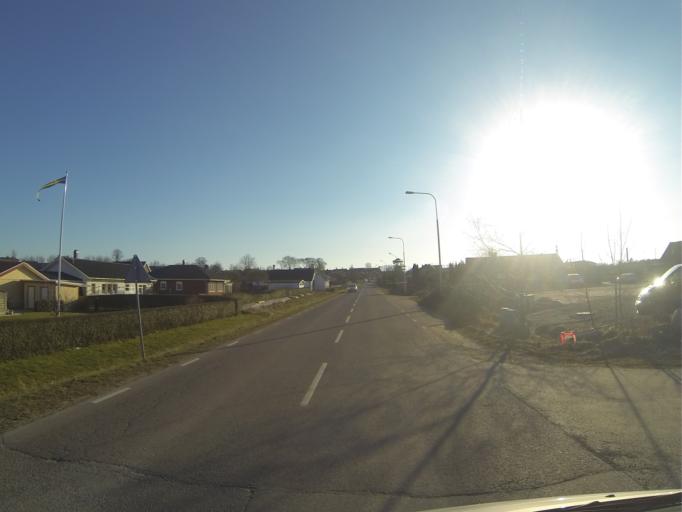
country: SE
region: Skane
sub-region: Hoors Kommun
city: Loberod
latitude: 55.7788
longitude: 13.5194
